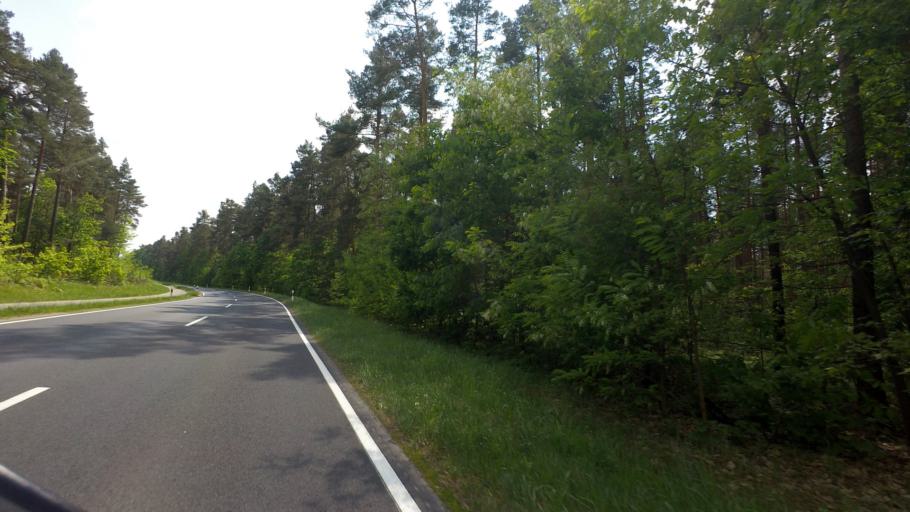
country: DE
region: Saxony
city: Niesky
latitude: 51.3091
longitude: 14.8257
